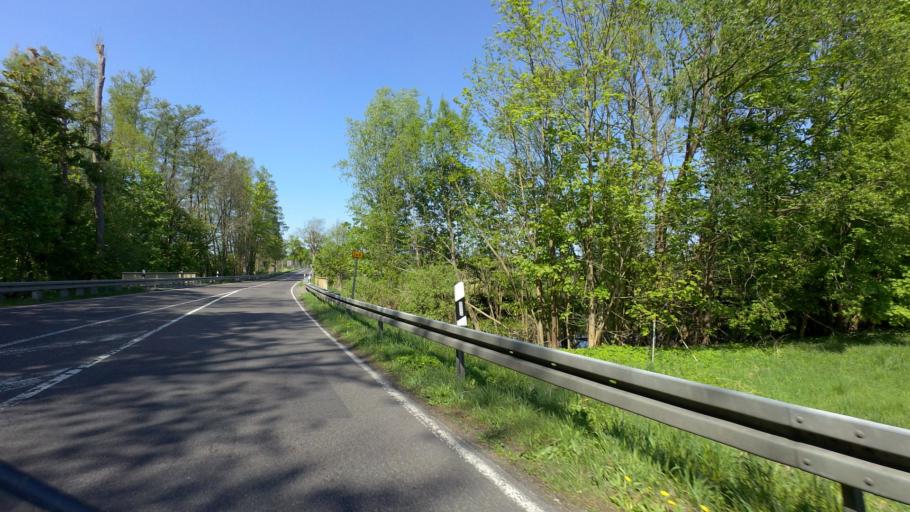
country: DE
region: Brandenburg
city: Friedland
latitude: 52.0872
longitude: 14.2592
